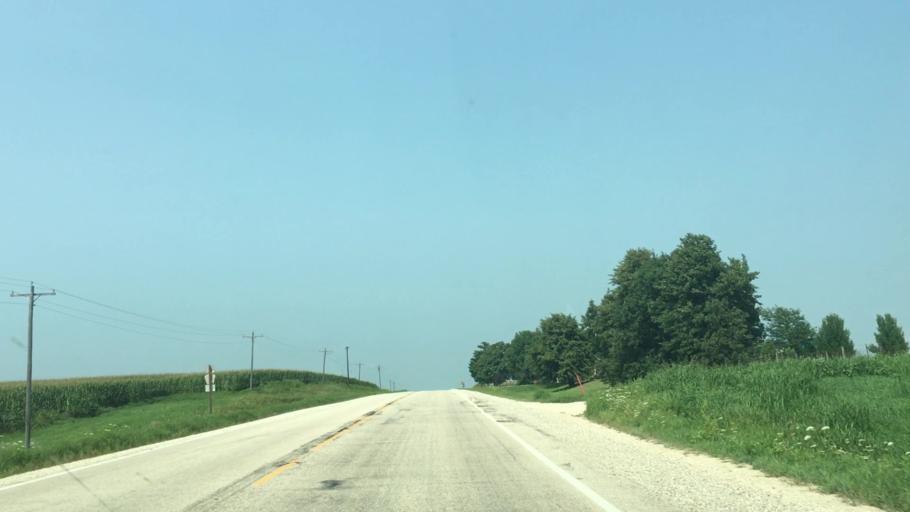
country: US
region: Iowa
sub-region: Fayette County
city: West Union
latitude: 43.0054
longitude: -91.8244
